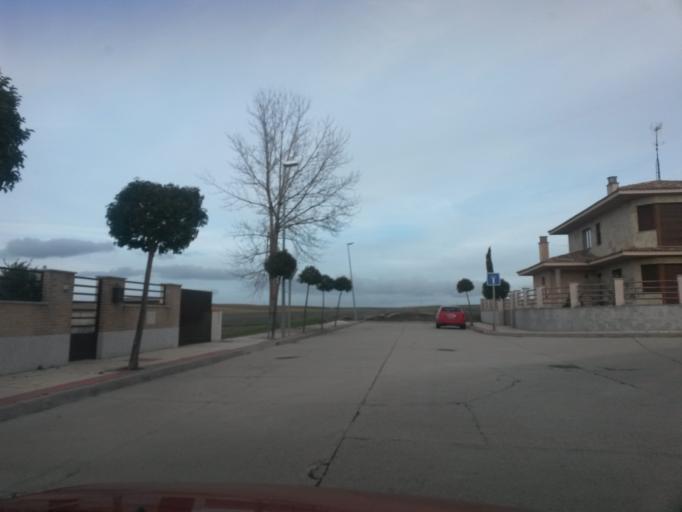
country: ES
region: Castille and Leon
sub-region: Provincia de Salamanca
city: Cabrerizos
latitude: 40.9842
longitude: -5.6089
